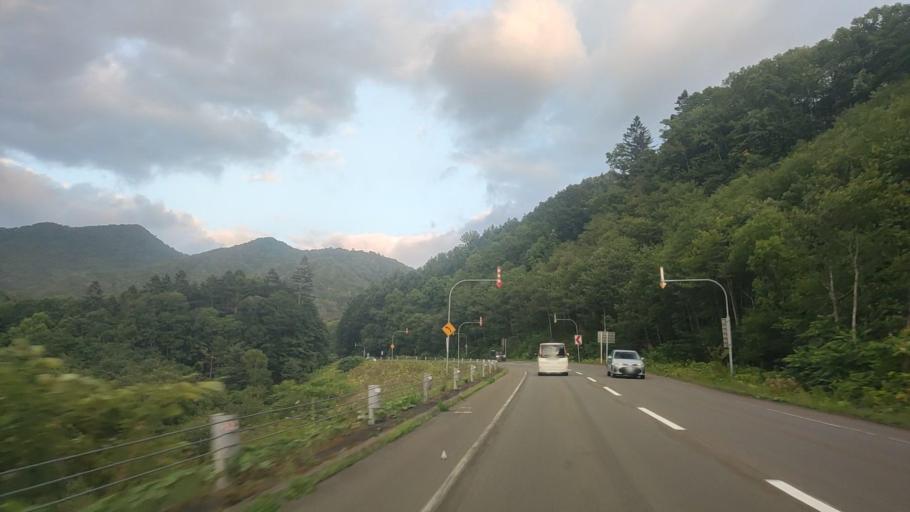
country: JP
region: Hokkaido
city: Ashibetsu
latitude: 43.3654
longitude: 142.2310
